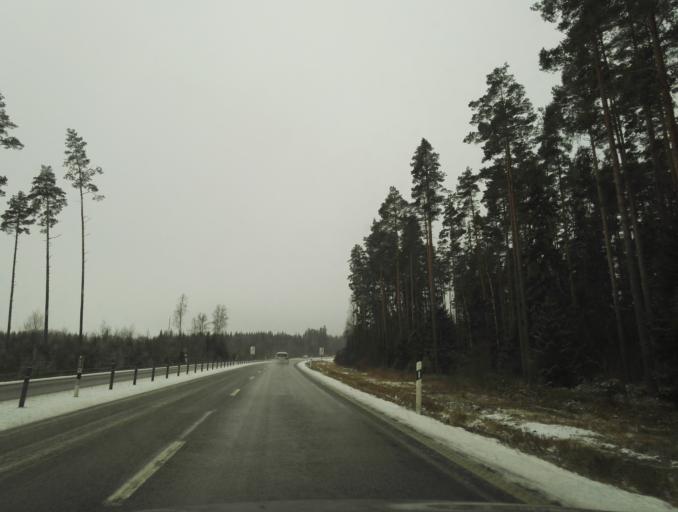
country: SE
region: Kronoberg
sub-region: Alvesta Kommun
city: Vislanda
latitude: 56.7566
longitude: 14.5220
